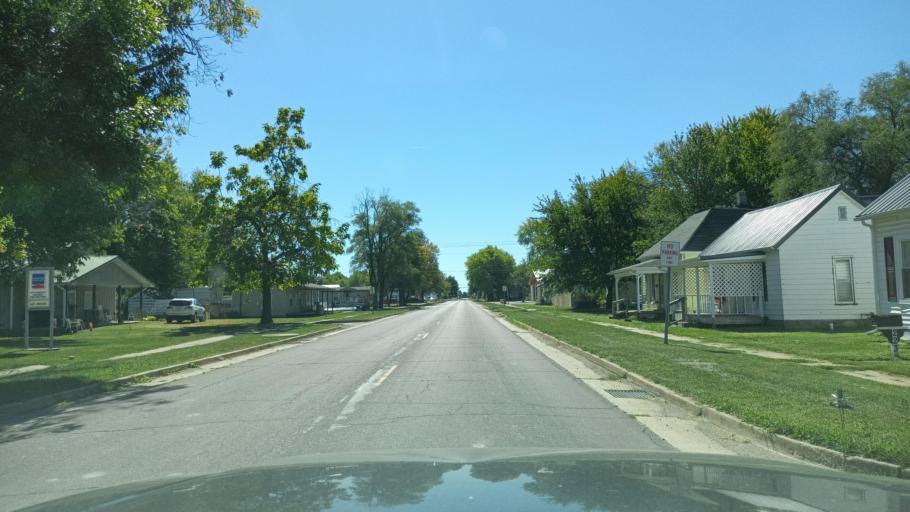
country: US
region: Missouri
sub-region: Macon County
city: La Plata
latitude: 40.0255
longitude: -92.4886
